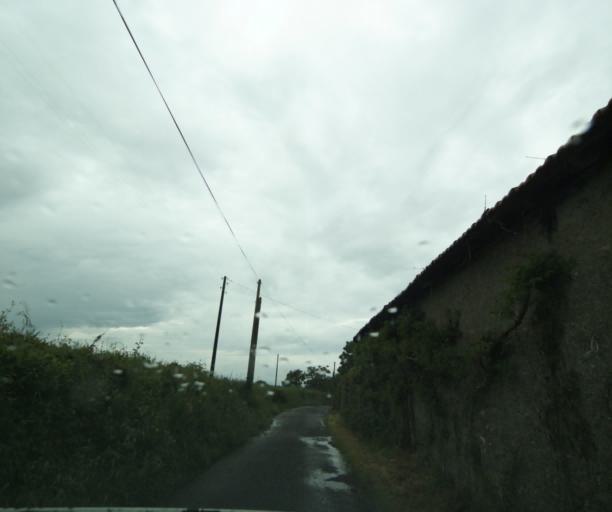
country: FR
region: Bourgogne
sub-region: Departement de Saone-et-Loire
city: Ciry-le-Noble
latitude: 46.5365
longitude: 4.2932
